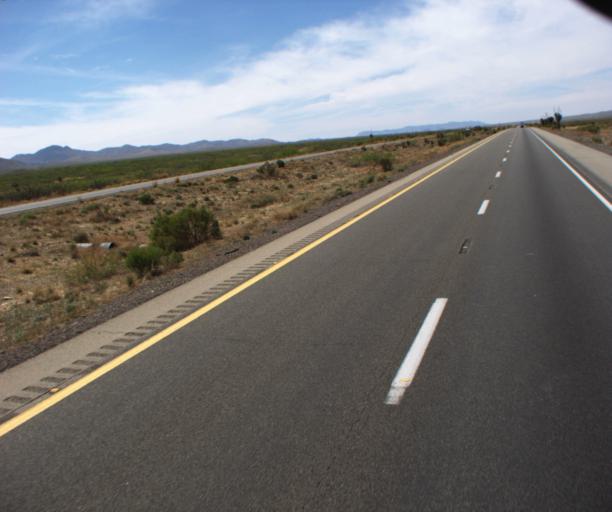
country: US
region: Arizona
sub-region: Cochise County
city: Willcox
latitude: 32.3394
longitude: -109.5561
